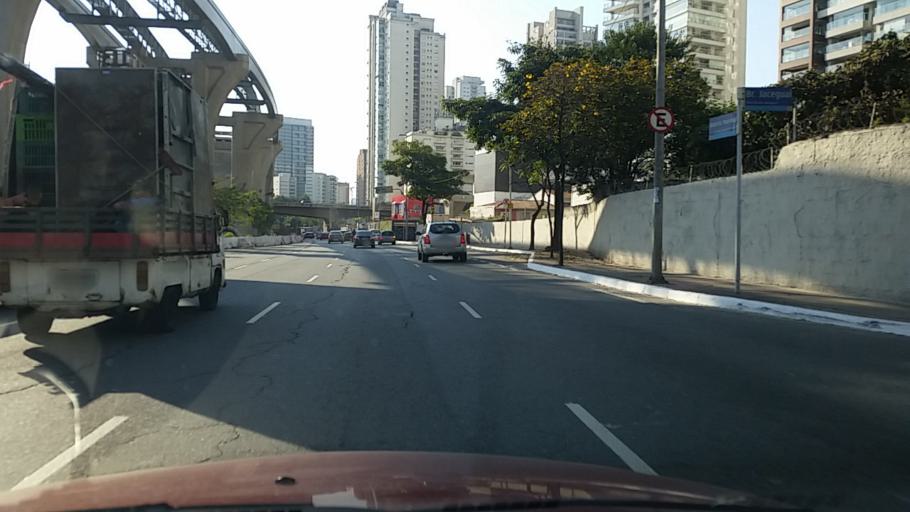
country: BR
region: Sao Paulo
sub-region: Diadema
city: Diadema
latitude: -23.6232
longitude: -46.6777
